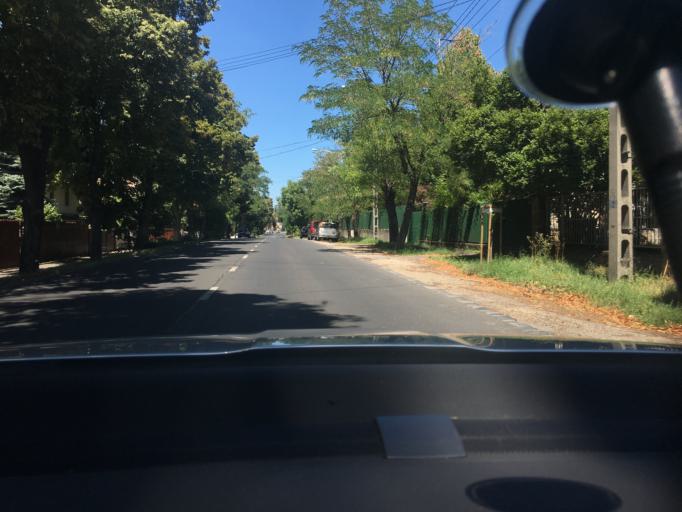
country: HU
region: Budapest
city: Budapest XVI. keruelet
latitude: 47.5064
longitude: 19.1812
